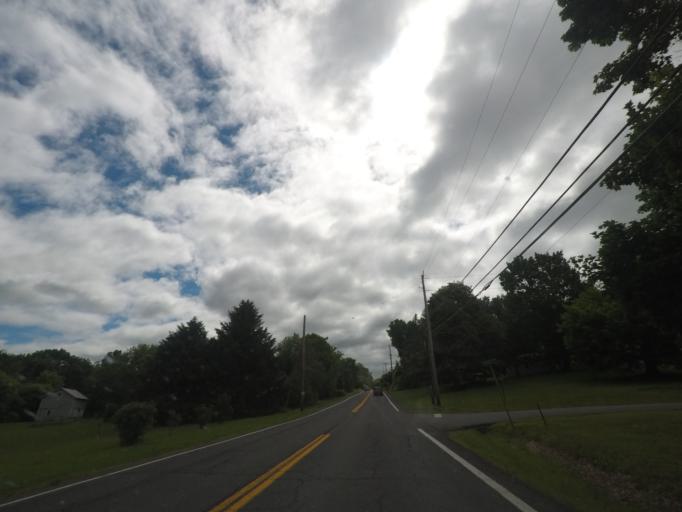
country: US
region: New York
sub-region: Columbia County
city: Philmont
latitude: 42.2416
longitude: -73.6862
